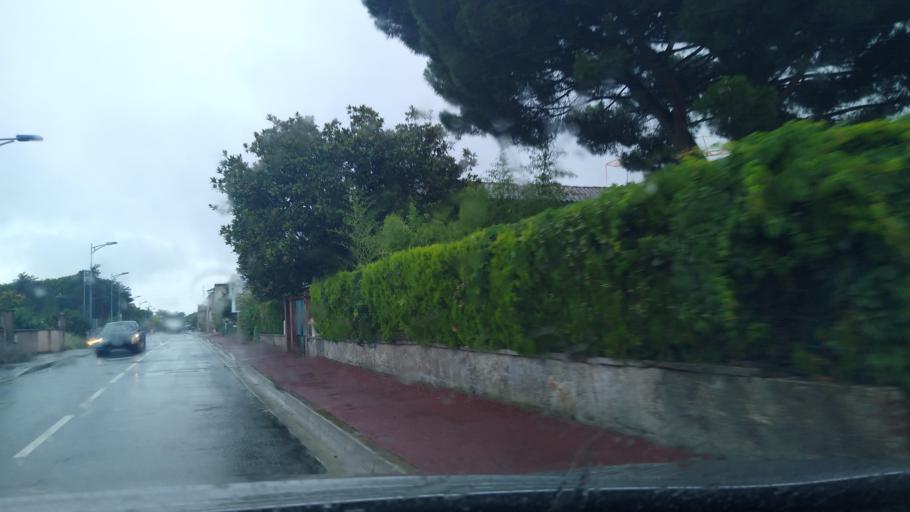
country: FR
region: Midi-Pyrenees
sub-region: Departement de la Haute-Garonne
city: Aucamville
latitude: 43.6592
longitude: 1.4350
